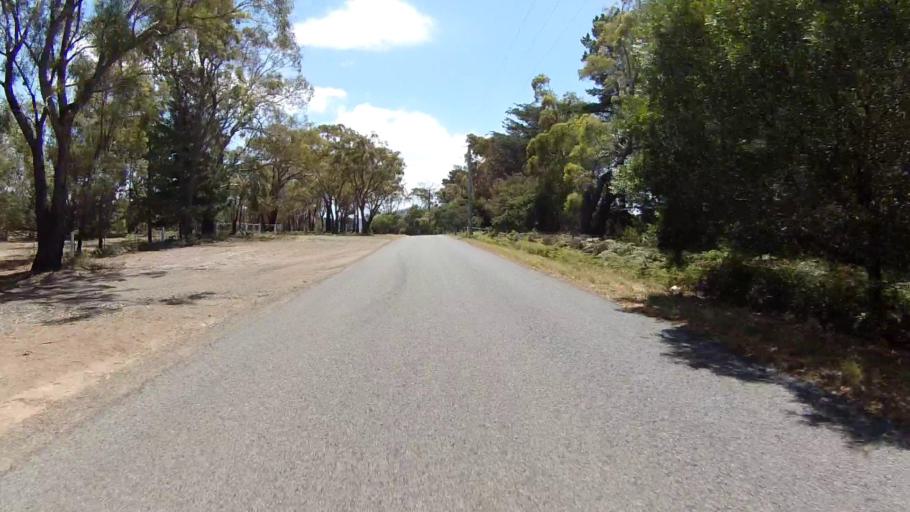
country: AU
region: Tasmania
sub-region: Clarence
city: Sandford
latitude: -42.9318
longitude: 147.4989
